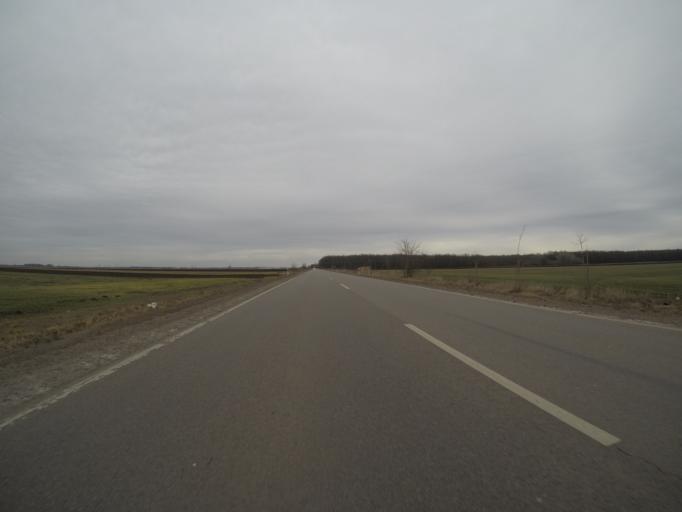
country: HU
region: Jasz-Nagykun-Szolnok
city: Jaszapati
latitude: 47.5112
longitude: 20.0786
